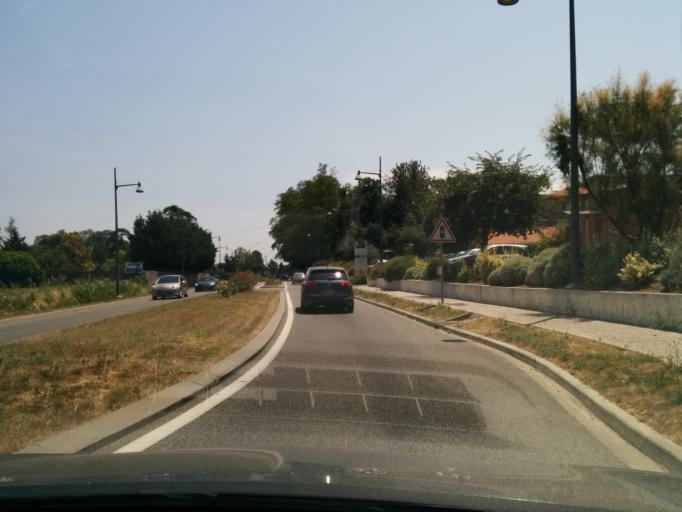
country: FR
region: Midi-Pyrenees
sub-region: Departement de la Haute-Garonne
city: Pompertuzat
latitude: 43.4955
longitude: 1.5192
